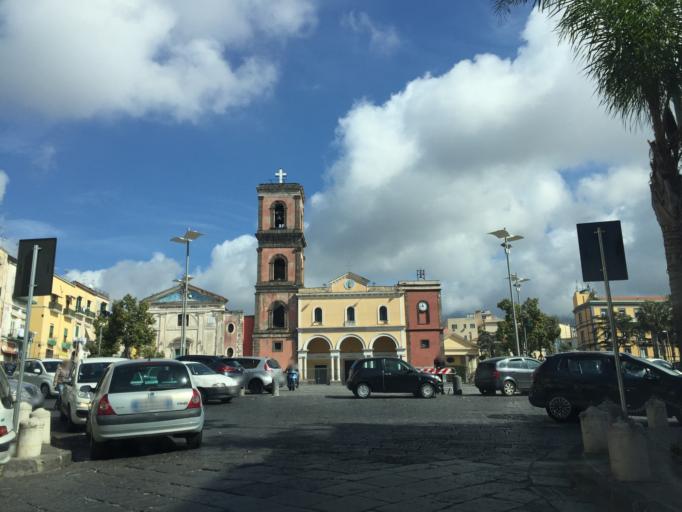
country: IT
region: Campania
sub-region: Provincia di Napoli
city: Ercolano
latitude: 40.8117
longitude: 14.3514
